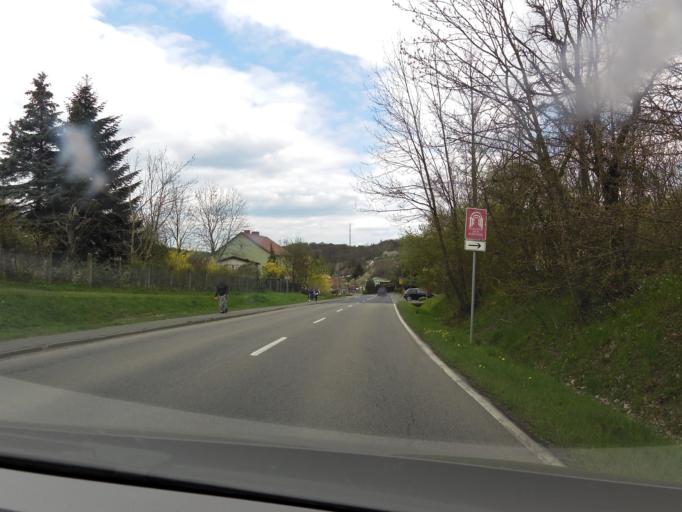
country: DE
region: Saxony-Anhalt
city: Eckartsberga
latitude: 51.1205
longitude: 11.5657
